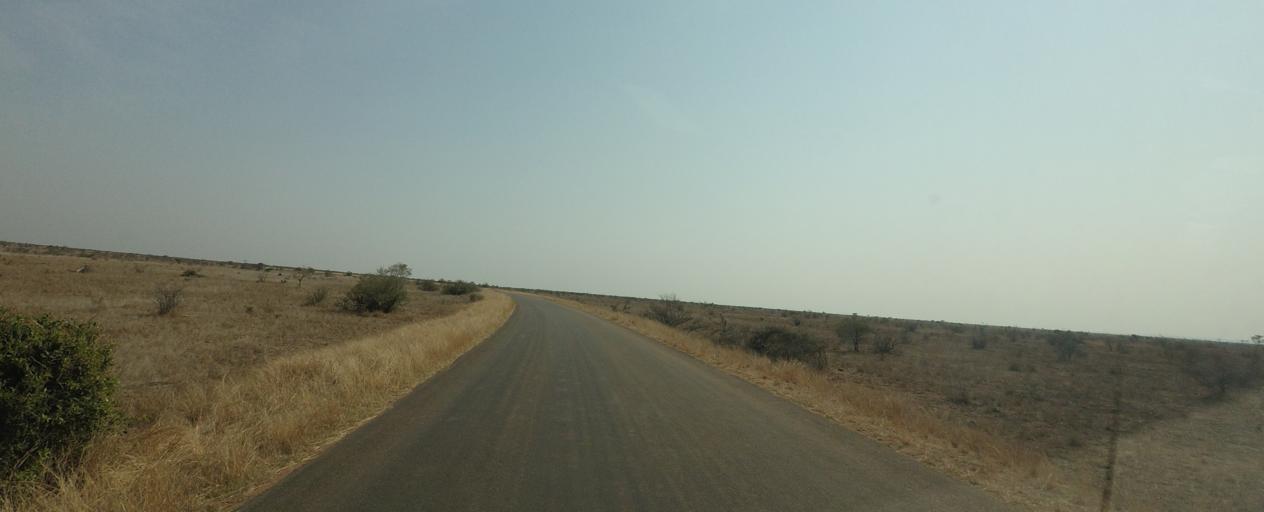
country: ZA
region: Limpopo
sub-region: Mopani District Municipality
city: Phalaborwa
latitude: -24.2644
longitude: 31.7306
